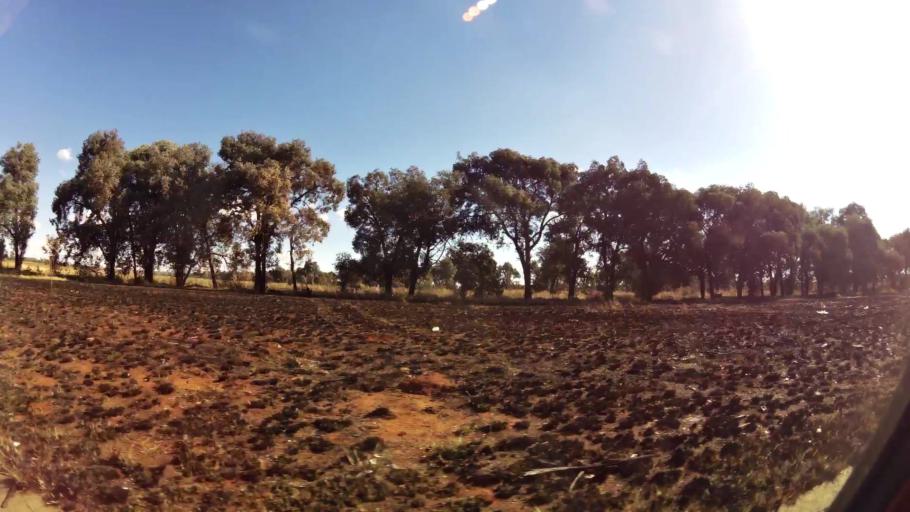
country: ZA
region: Gauteng
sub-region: West Rand District Municipality
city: Carletonville
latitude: -26.3690
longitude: 27.3779
